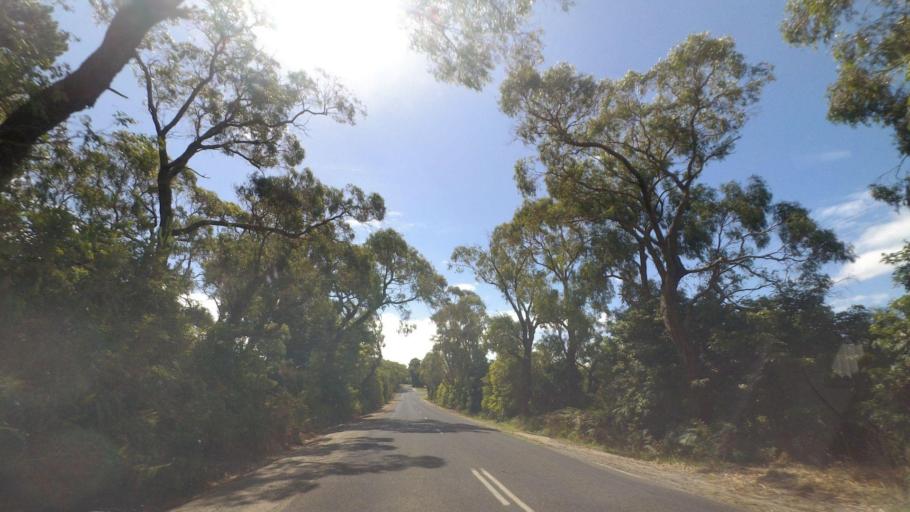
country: AU
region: Victoria
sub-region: Cardinia
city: Koo-Wee-Rup
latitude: -38.3174
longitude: 145.6678
